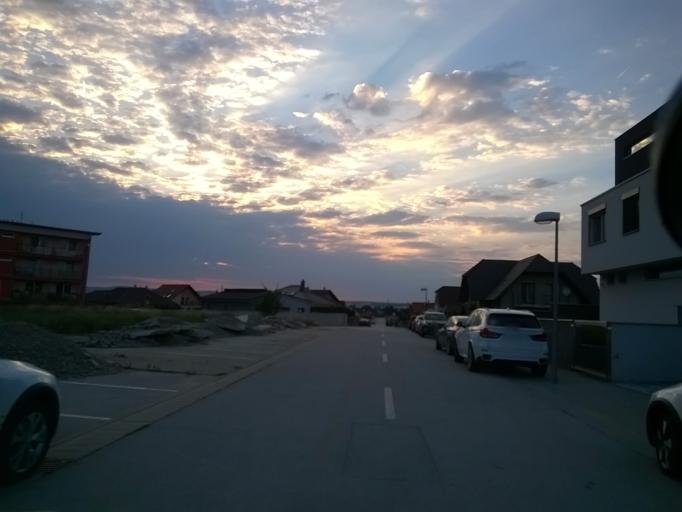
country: SK
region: Trnavsky
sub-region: Okres Senica
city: Senica
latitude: 48.6872
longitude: 17.3820
